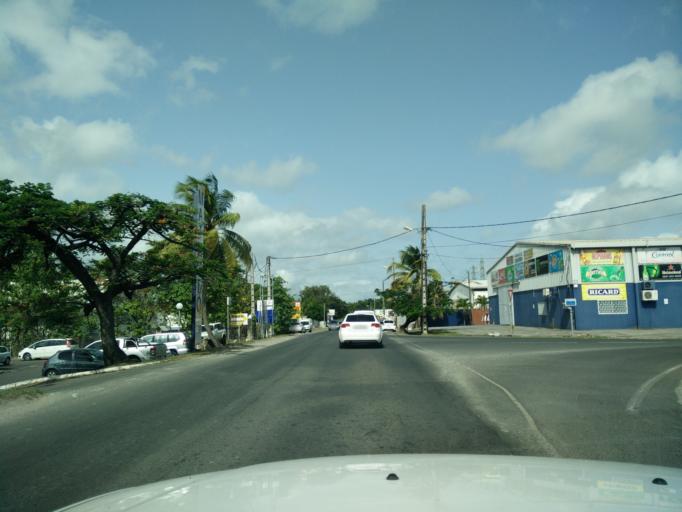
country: GP
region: Guadeloupe
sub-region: Guadeloupe
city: Pointe-a-Pitre
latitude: 16.2458
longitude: -61.5576
